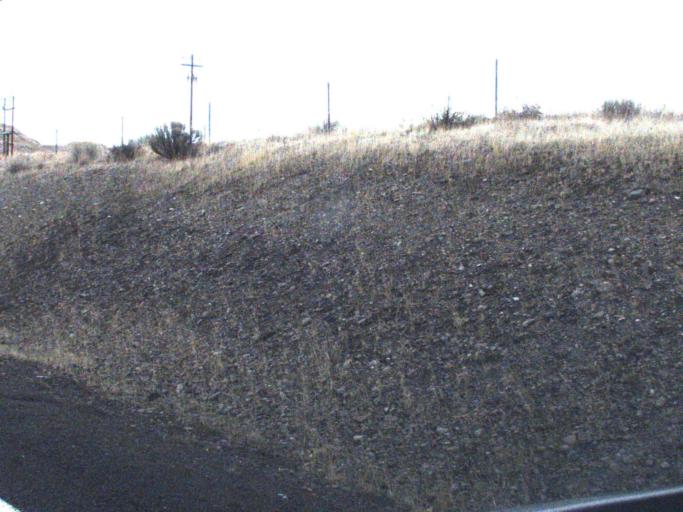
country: US
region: Washington
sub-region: Walla Walla County
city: Waitsburg
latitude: 46.5831
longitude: -118.2165
